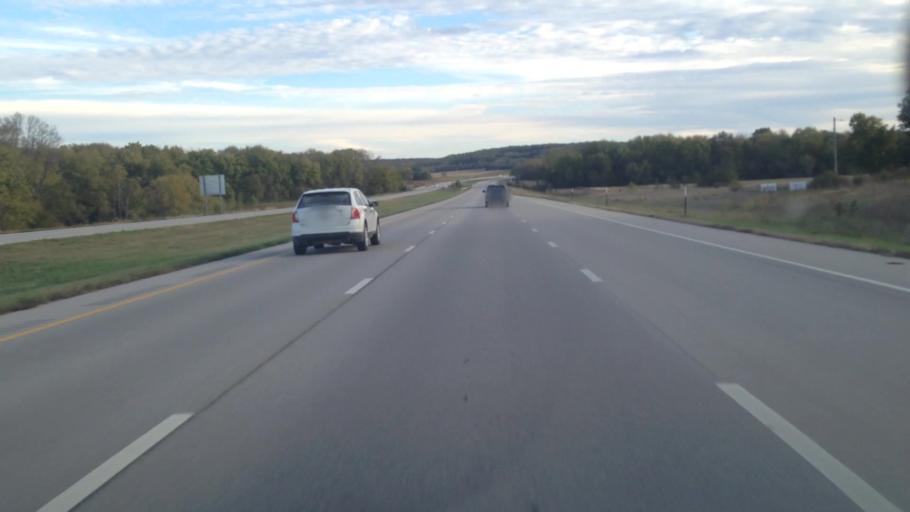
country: US
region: Kansas
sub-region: Douglas County
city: Lawrence
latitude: 38.8813
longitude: -95.2576
